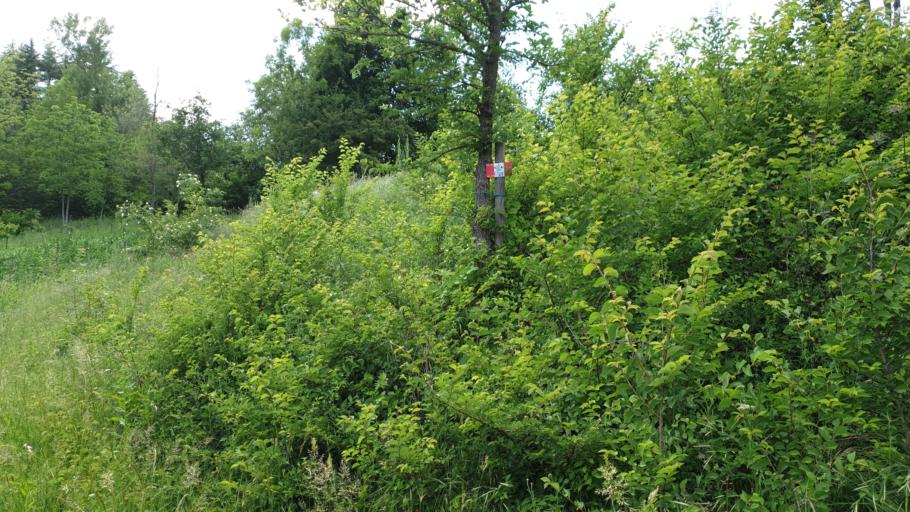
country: IT
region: Emilia-Romagna
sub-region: Provincia di Bologna
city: Sasso Marconi
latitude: 44.3883
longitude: 11.2749
